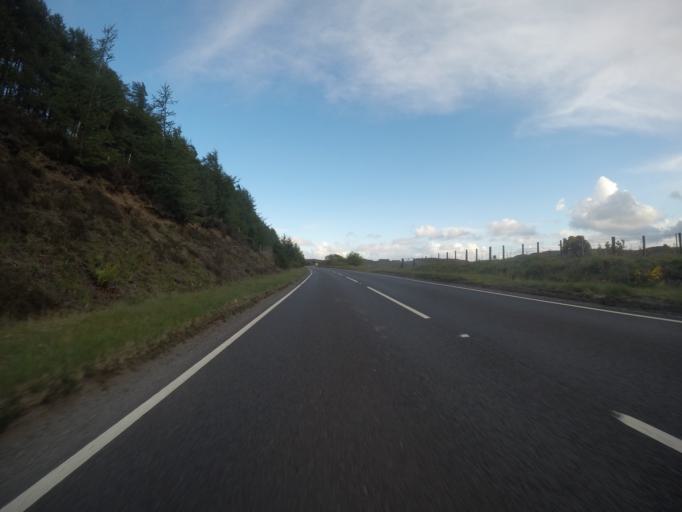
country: GB
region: Scotland
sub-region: Highland
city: Portree
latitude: 57.5270
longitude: -6.3471
